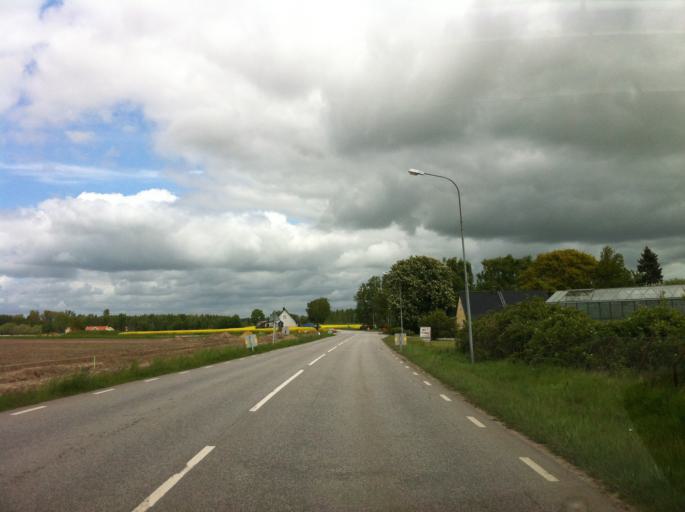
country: SE
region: Skane
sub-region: Svalovs Kommun
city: Teckomatorp
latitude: 55.8407
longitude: 13.1018
